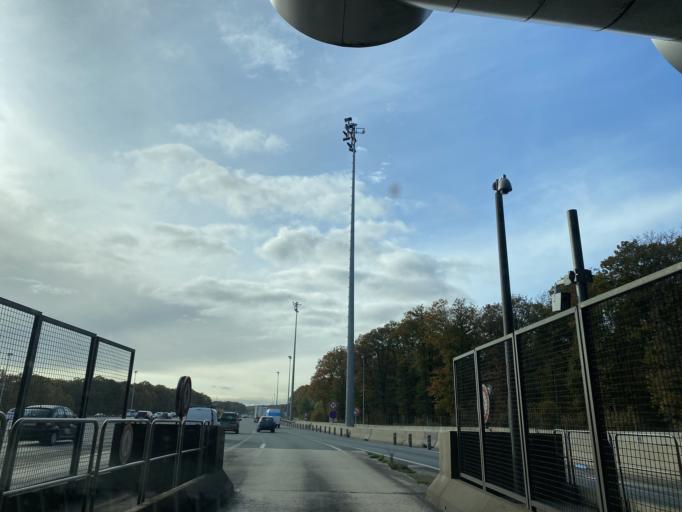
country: FR
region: Ile-de-France
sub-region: Departement des Yvelines
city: Saint-Arnoult-en-Yvelines
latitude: 48.5541
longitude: 1.9299
